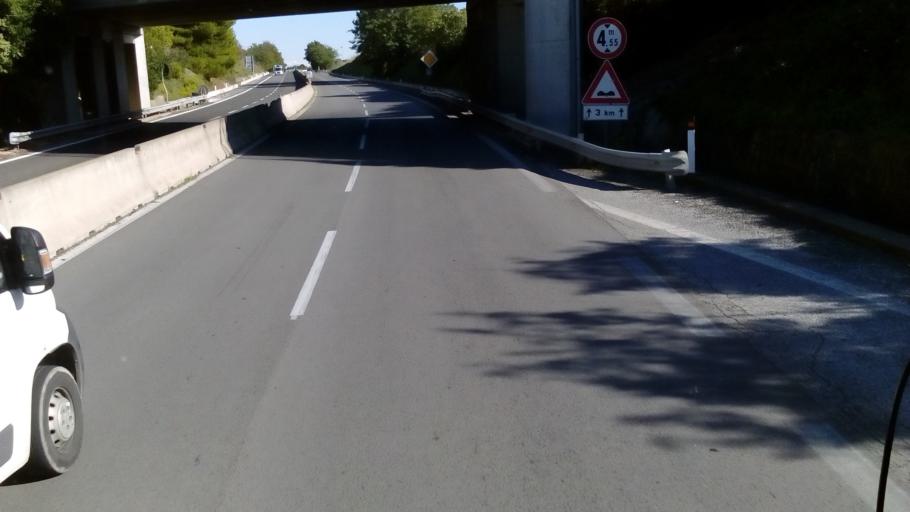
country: IT
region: Latium
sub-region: Provincia di Viterbo
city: Montalto di Castro
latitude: 42.3477
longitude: 11.6043
